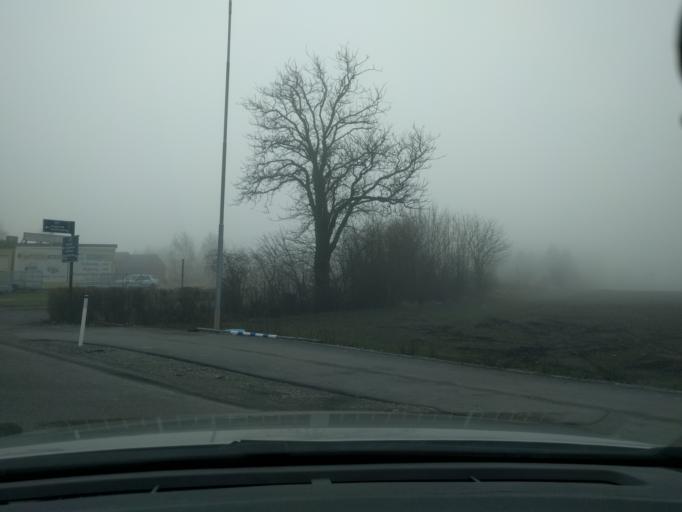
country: SE
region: Skane
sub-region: Malmo
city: Bunkeflostrand
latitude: 55.5578
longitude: 12.9685
